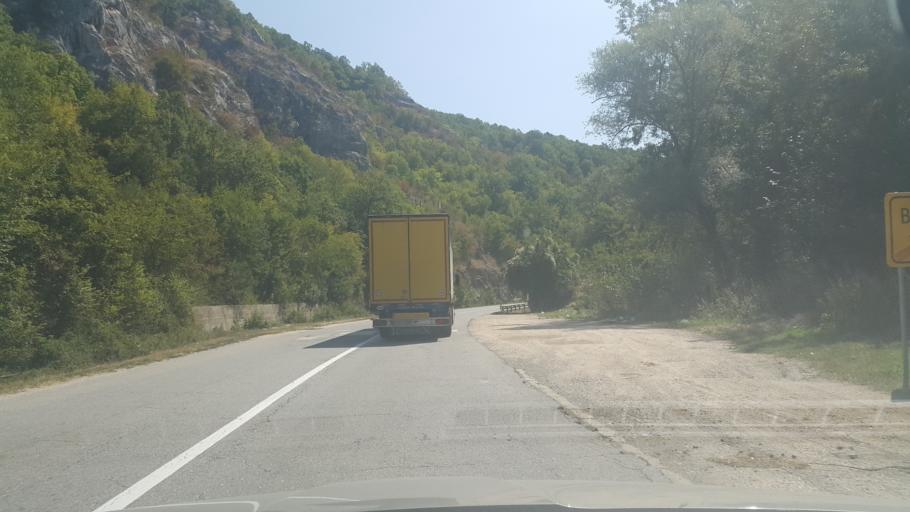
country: RS
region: Central Serbia
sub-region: Zajecarski Okrug
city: Zajecar
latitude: 43.7805
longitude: 22.3110
